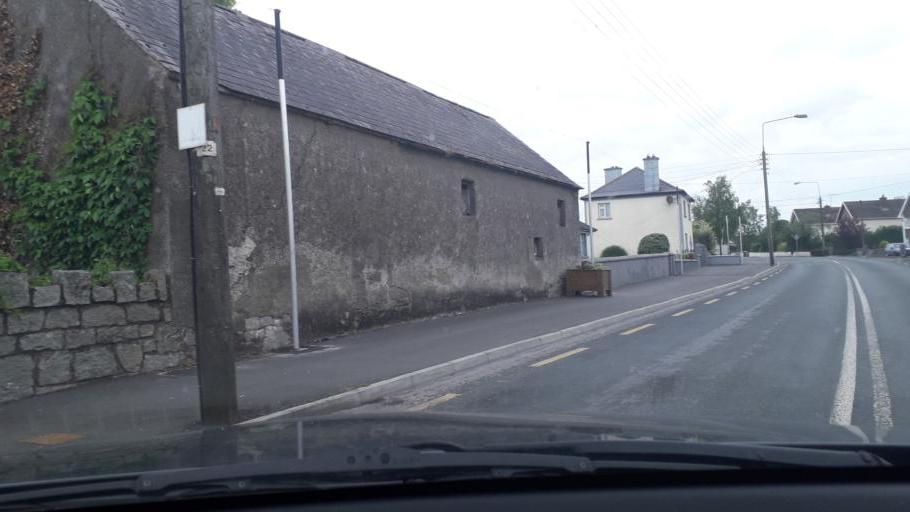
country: IE
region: Leinster
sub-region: Kildare
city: Castledermot
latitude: 52.9137
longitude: -6.8372
